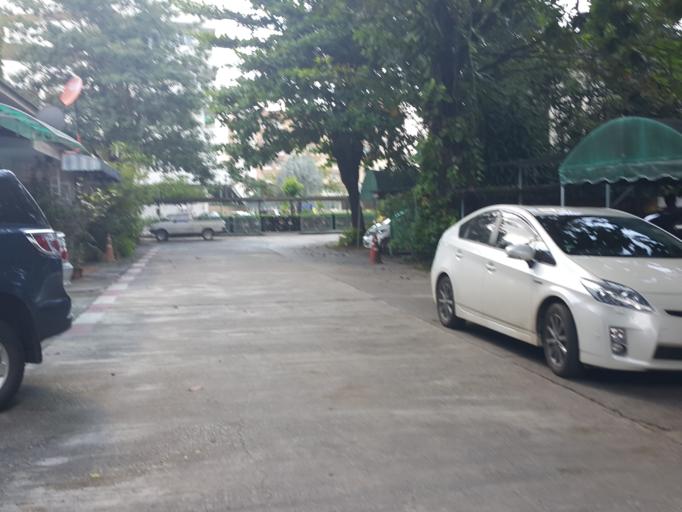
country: TH
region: Lampang
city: Lampang
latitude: 18.2886
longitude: 99.5072
